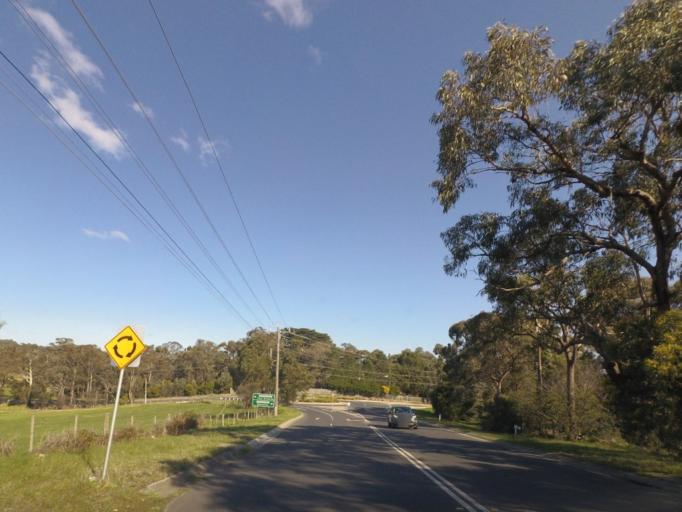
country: AU
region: Victoria
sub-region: Manningham
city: Park Orchards
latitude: -37.7708
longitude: 145.1998
